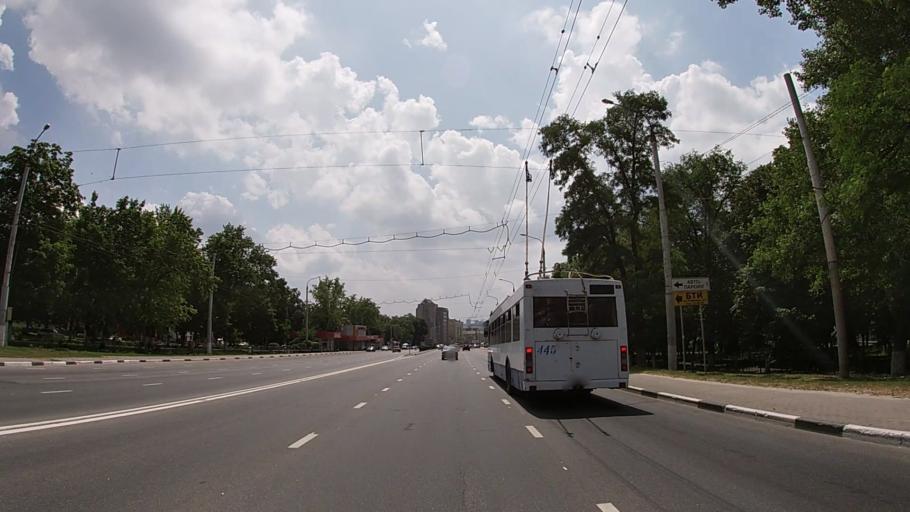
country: RU
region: Belgorod
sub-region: Belgorodskiy Rayon
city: Belgorod
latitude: 50.6064
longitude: 36.5803
